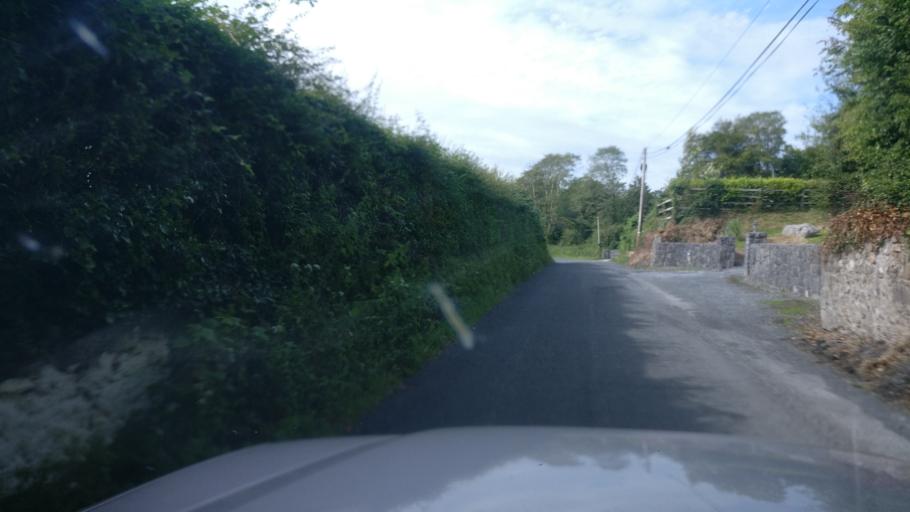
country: IE
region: Connaught
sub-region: County Galway
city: Gort
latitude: 53.1080
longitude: -8.7332
